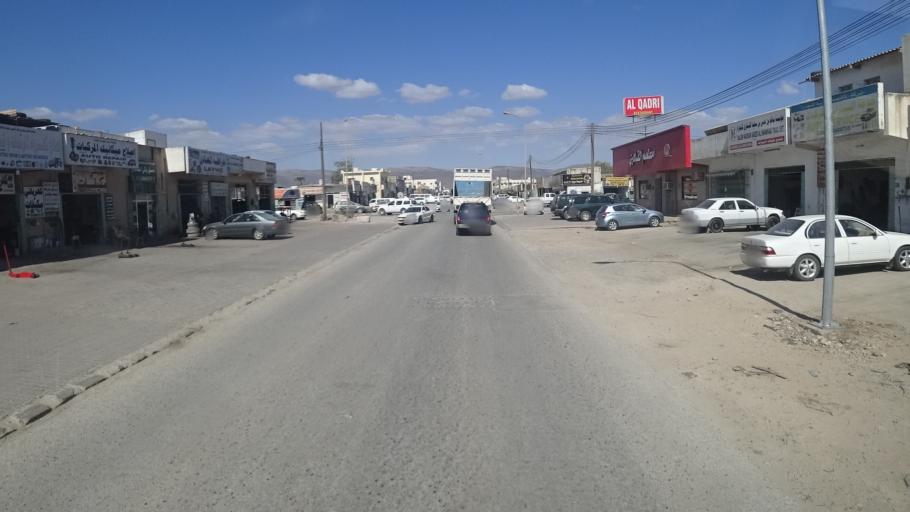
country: OM
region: Zufar
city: Salalah
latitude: 17.0171
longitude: 54.0539
